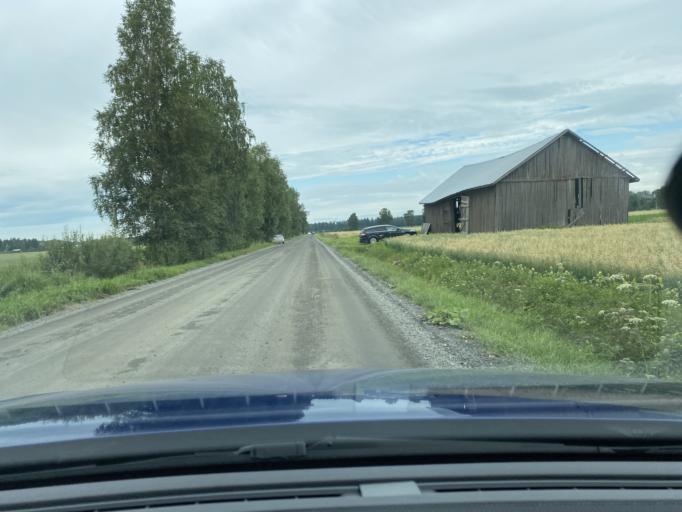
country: FI
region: Satakunta
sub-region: Rauma
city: Kiukainen
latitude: 61.1462
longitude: 21.9996
